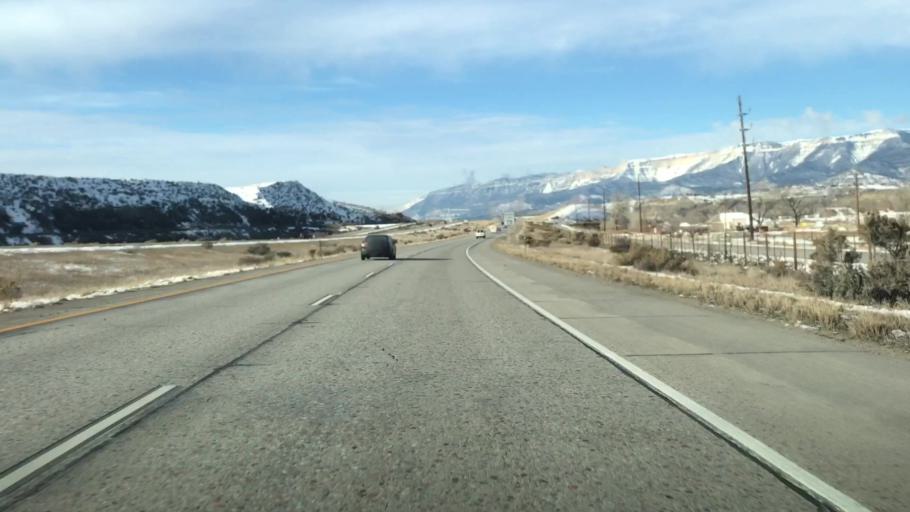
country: US
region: Colorado
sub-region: Garfield County
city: Rifle
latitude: 39.5303
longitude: -107.7275
